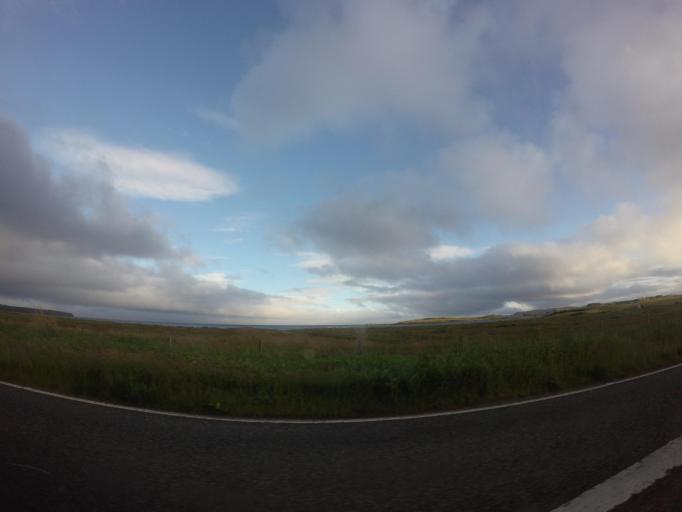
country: GB
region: Scotland
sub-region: Eilean Siar
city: Stornoway
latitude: 58.2041
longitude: -6.3171
